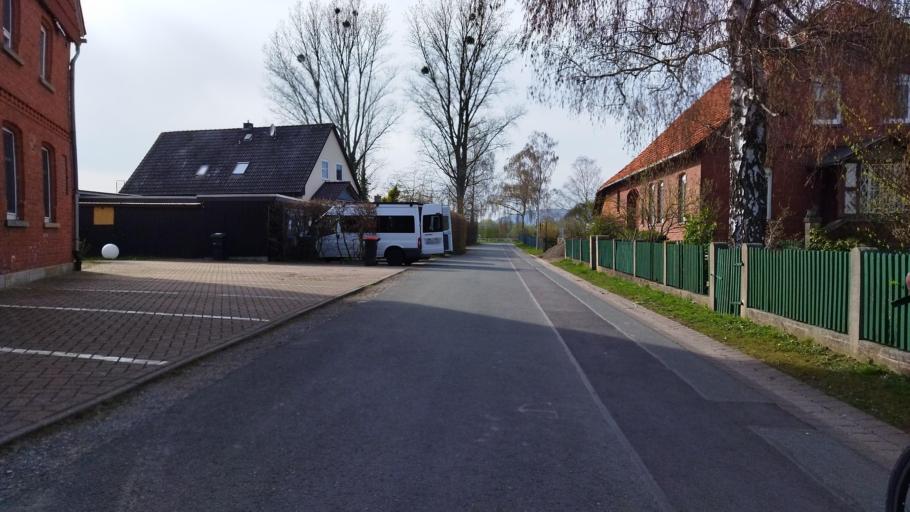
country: DE
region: Lower Saxony
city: Buchholz
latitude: 52.1789
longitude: 9.1612
